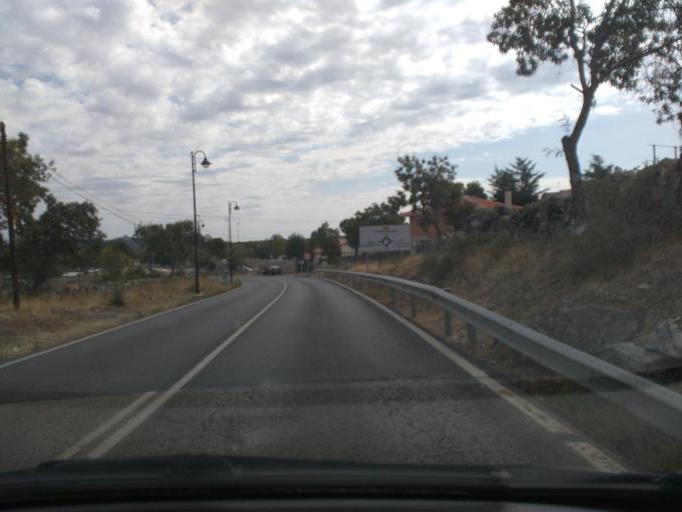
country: ES
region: Madrid
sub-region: Provincia de Madrid
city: Galapagar
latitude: 40.5771
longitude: -3.9916
